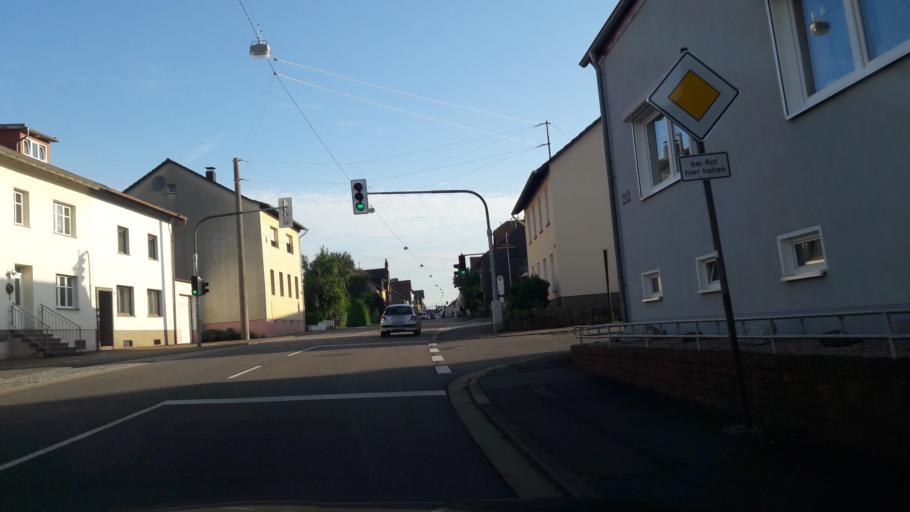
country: DE
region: Saarland
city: Riegelsberg
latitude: 49.3153
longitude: 6.9402
